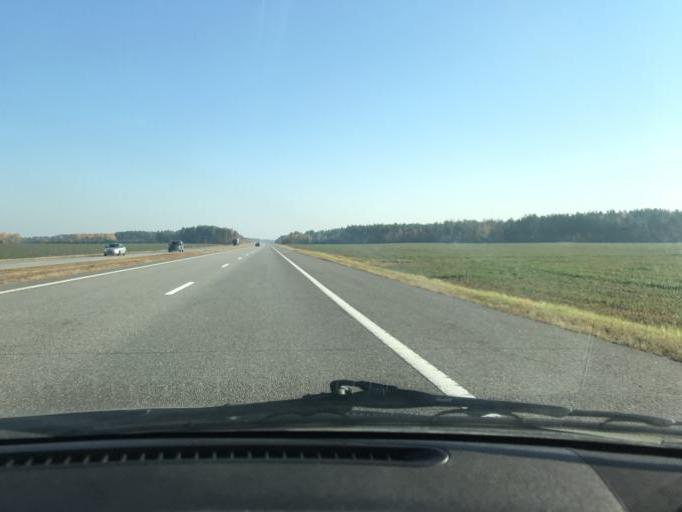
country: BY
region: Minsk
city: Bobr
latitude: 54.3871
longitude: 29.3782
